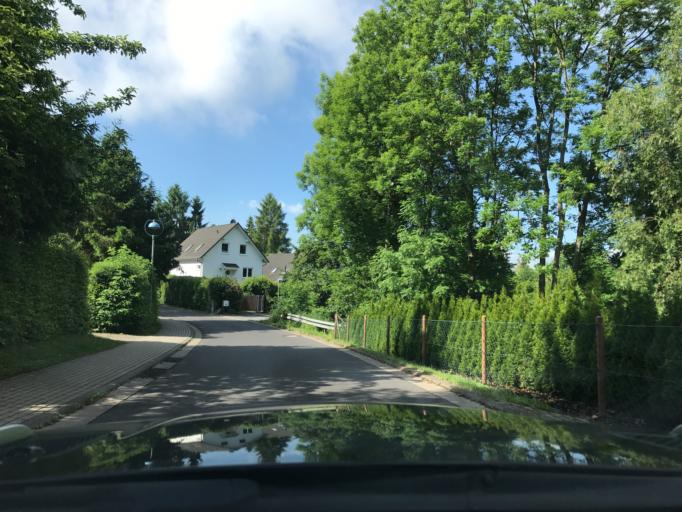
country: DE
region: Thuringia
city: Muehlhausen
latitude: 51.2014
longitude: 10.4402
